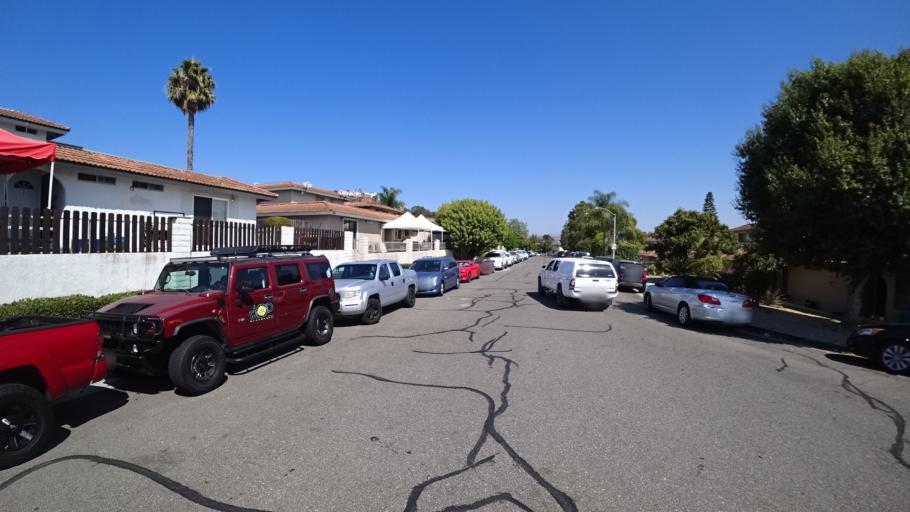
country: US
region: California
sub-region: Orange County
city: San Clemente
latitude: 33.4549
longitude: -117.6458
